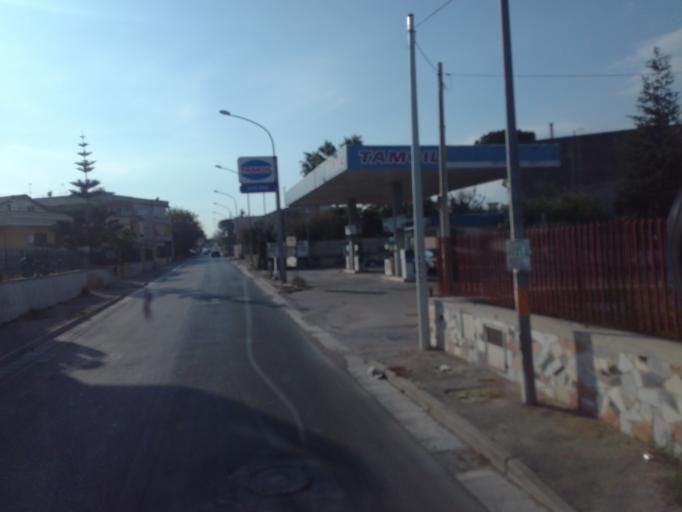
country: IT
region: Campania
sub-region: Provincia di Napoli
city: Giugliano in Campania
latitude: 40.9435
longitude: 14.1805
